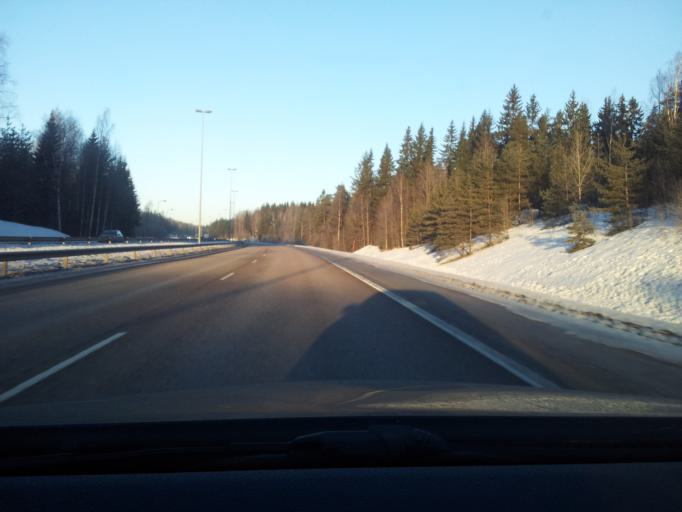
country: FI
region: Uusimaa
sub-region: Helsinki
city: Espoo
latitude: 60.2446
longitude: 24.5660
